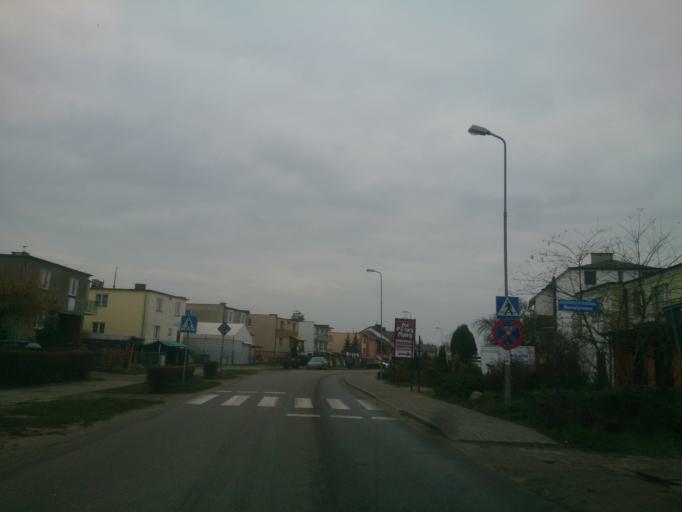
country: PL
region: West Pomeranian Voivodeship
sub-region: Powiat slawienski
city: Darlowo
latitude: 54.3805
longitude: 16.3197
